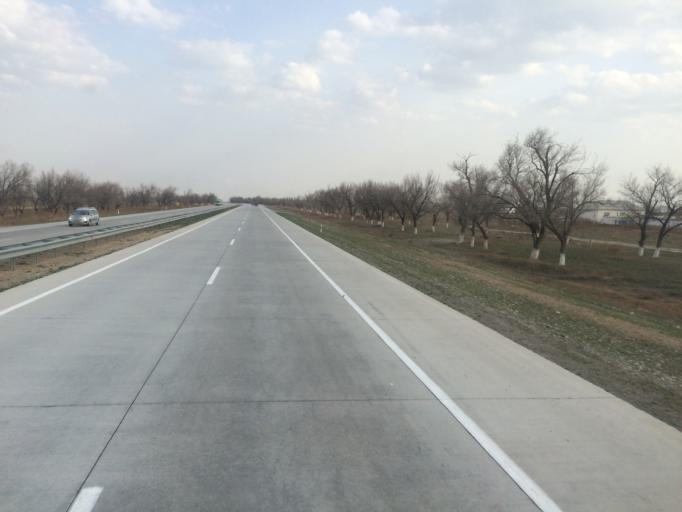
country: KZ
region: Ongtustik Qazaqstan
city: Bayaldyr
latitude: 43.0148
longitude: 68.7610
